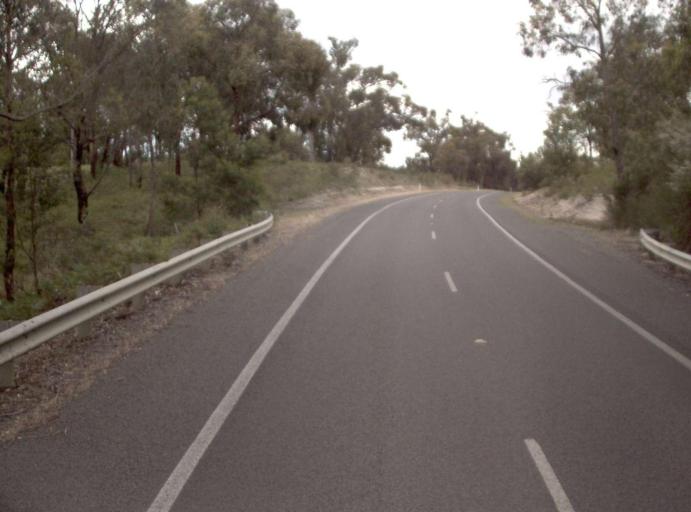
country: AU
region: Victoria
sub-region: Wellington
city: Sale
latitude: -38.3269
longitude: 147.0182
